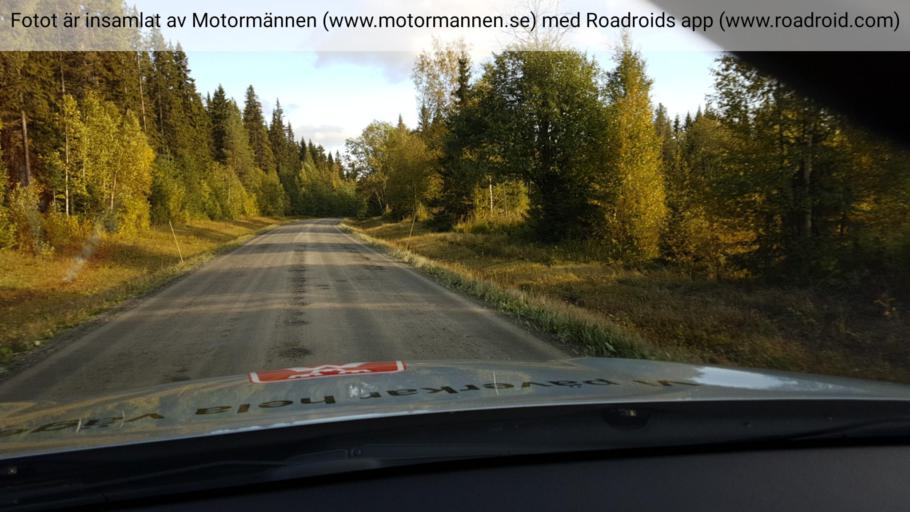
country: SE
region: Jaemtland
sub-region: Krokoms Kommun
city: Krokom
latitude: 63.6993
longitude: 14.5574
